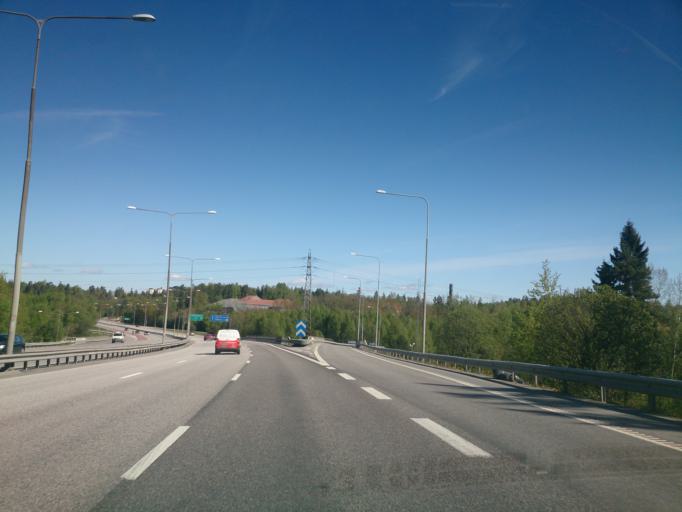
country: SE
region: Stockholm
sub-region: Haninge Kommun
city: Handen
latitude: 59.2170
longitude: 18.1352
